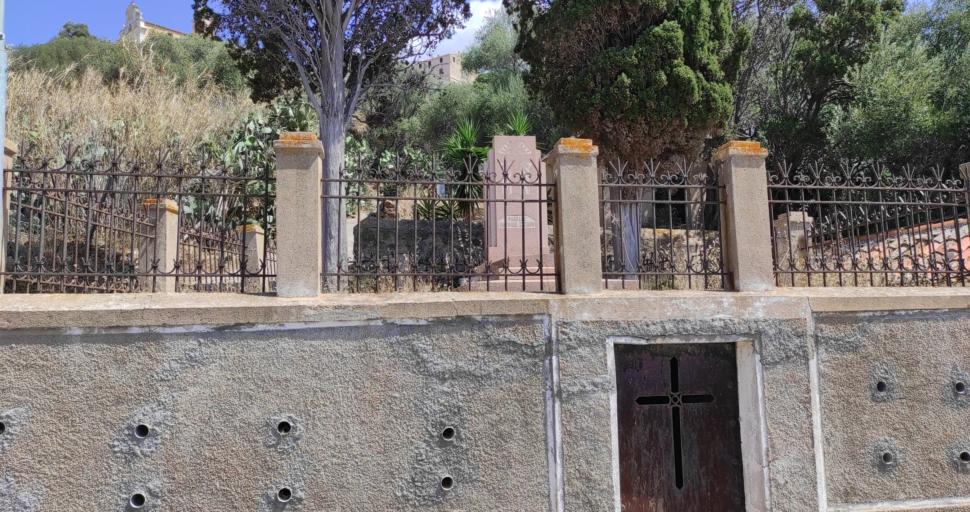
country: FR
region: Corsica
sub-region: Departement de la Corse-du-Sud
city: Cargese
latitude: 42.1323
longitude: 8.5961
